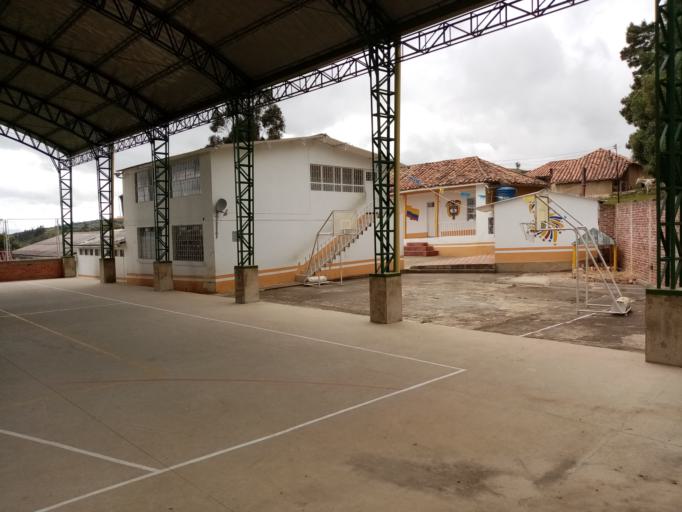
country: CO
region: Boyaca
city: Toca
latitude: 5.6082
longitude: -73.2351
